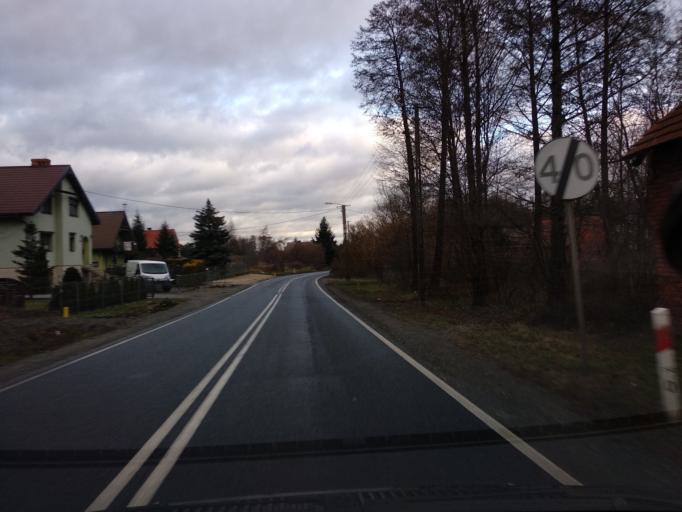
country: PL
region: Lower Silesian Voivodeship
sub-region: Powiat olesnicki
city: Miedzyborz
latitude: 51.3847
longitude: 17.6456
